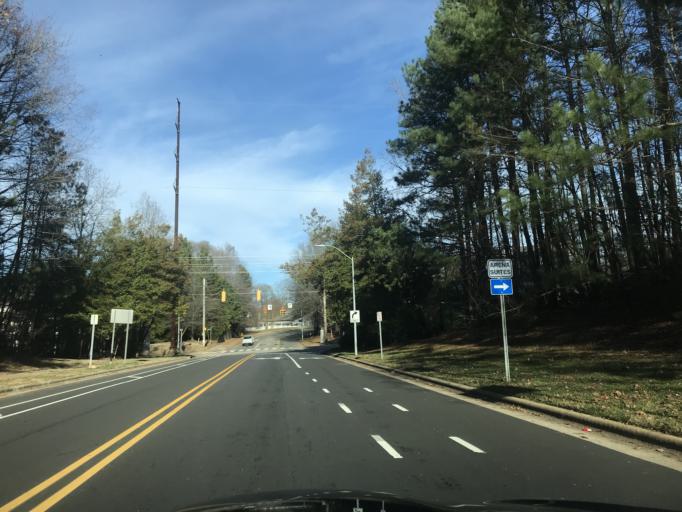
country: US
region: North Carolina
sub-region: Wake County
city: Cary
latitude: 35.8029
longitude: -78.7349
